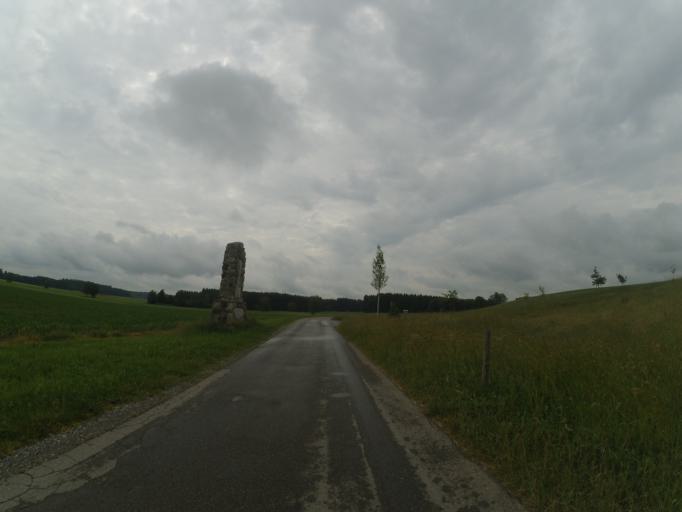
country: DE
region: Baden-Wuerttemberg
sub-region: Tuebingen Region
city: Kisslegg
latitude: 47.7553
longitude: 9.8518
